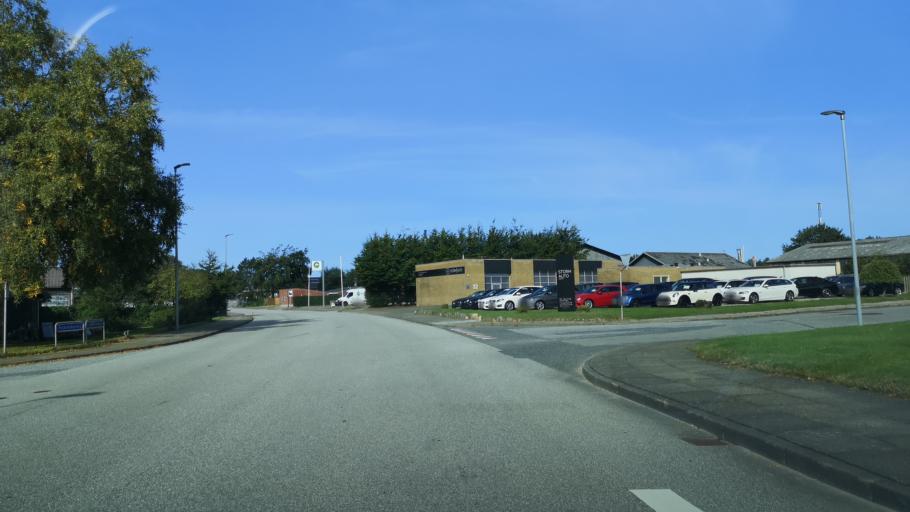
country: DK
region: Central Jutland
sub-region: Herning Kommune
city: Herning
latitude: 56.1526
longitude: 8.9833
